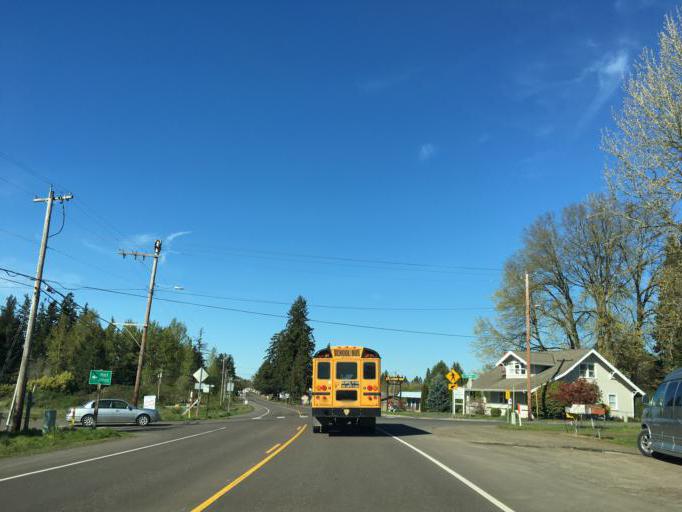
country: US
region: Oregon
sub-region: Marion County
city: Hubbard
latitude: 45.2230
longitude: -122.7589
